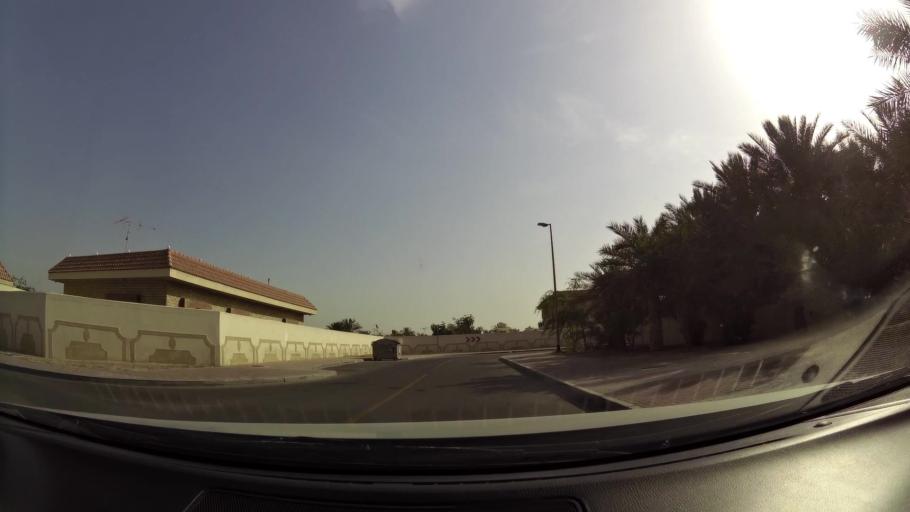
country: AE
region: Ash Shariqah
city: Sharjah
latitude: 25.2164
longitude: 55.3947
